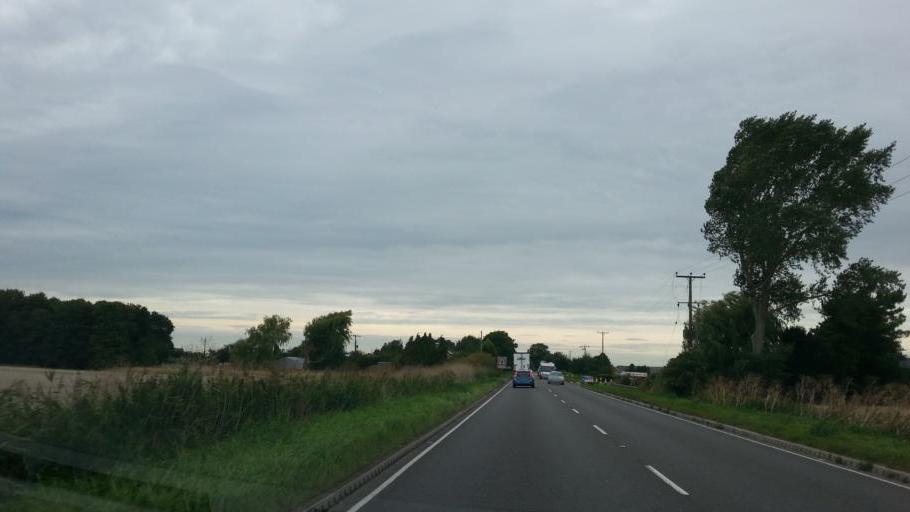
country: GB
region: England
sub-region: Cambridgeshire
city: March
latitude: 52.6138
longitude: 0.0053
